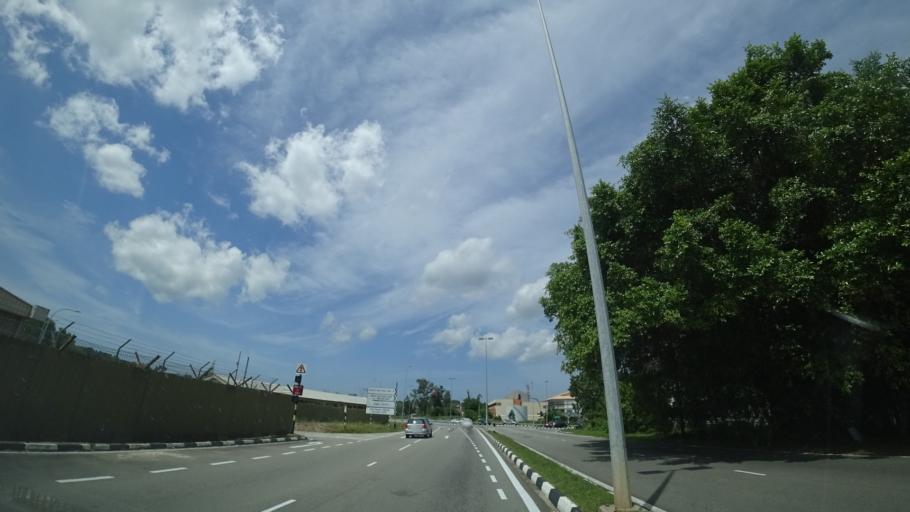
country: BN
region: Brunei and Muara
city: Bandar Seri Begawan
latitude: 4.9058
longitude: 114.9103
